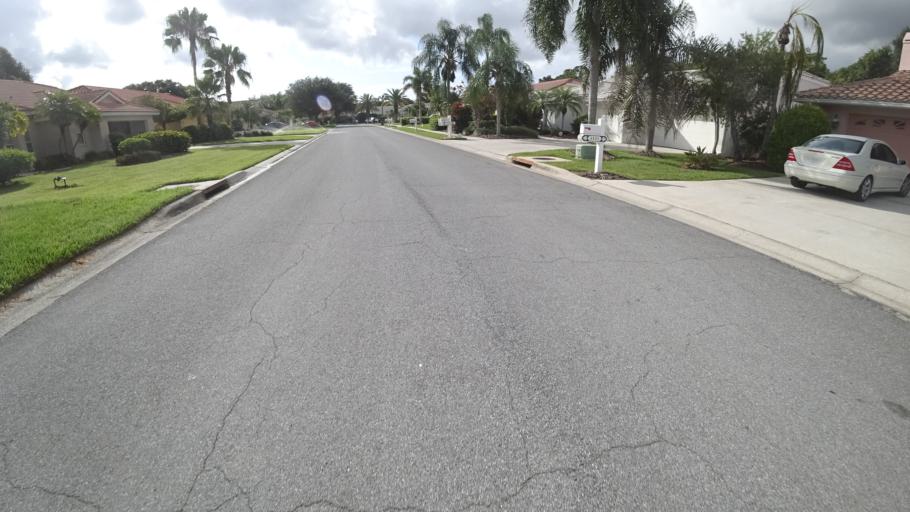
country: US
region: Florida
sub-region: Sarasota County
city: Desoto Lakes
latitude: 27.4148
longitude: -82.4837
